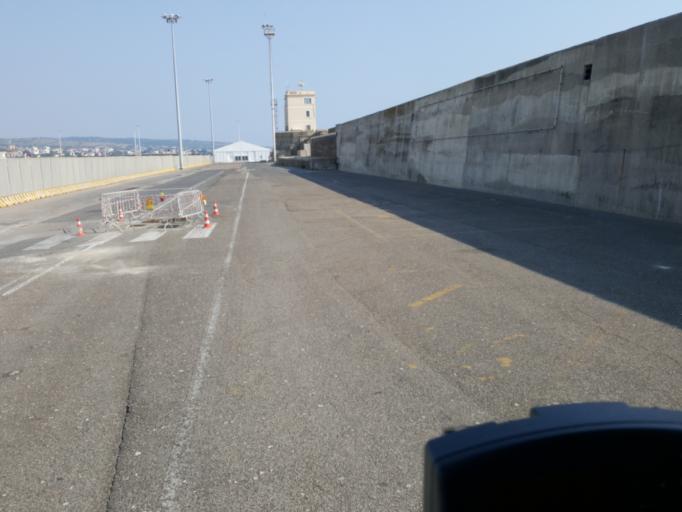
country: IT
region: Latium
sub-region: Citta metropolitana di Roma Capitale
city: Civitavecchia
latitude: 42.0921
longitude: 11.7834
